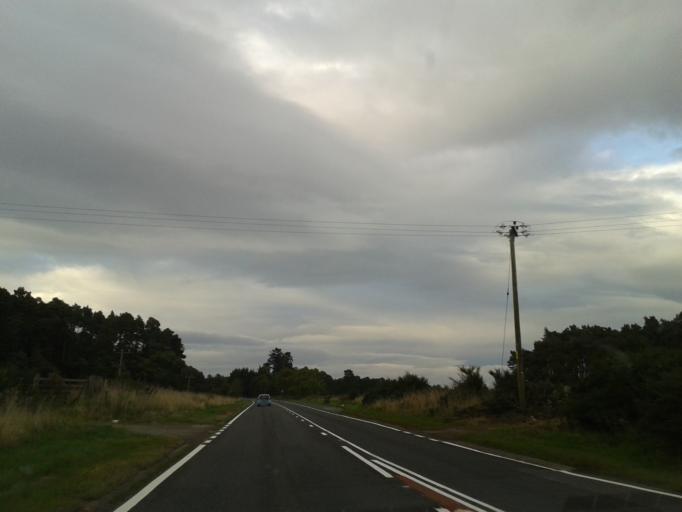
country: GB
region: Scotland
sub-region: Highland
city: Inverness
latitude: 57.4517
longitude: -4.2804
